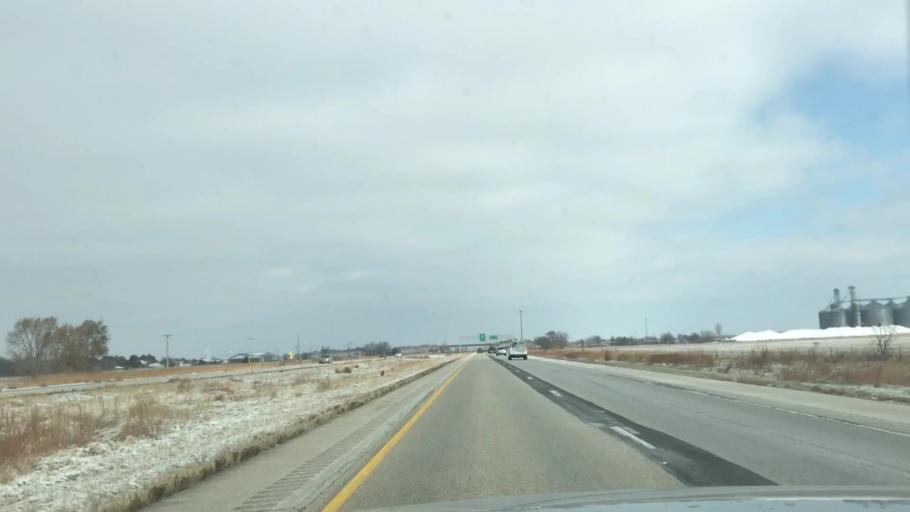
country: US
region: Illinois
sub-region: Sangamon County
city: Divernon
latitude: 39.5587
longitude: -89.6458
